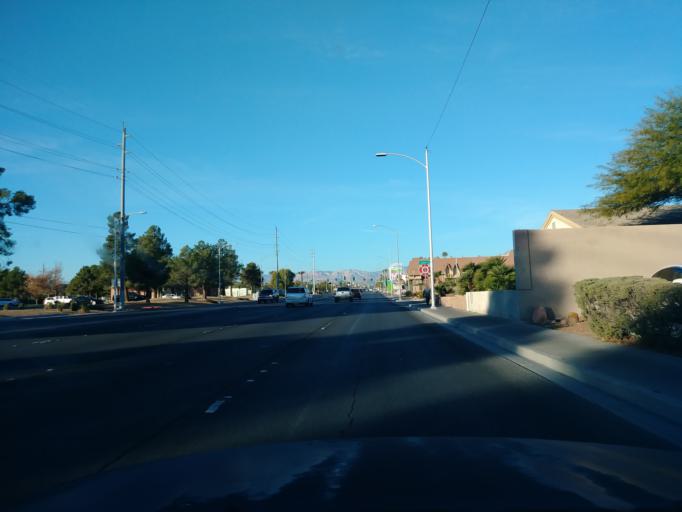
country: US
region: Nevada
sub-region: Clark County
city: Spring Valley
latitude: 36.1593
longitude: -115.2276
